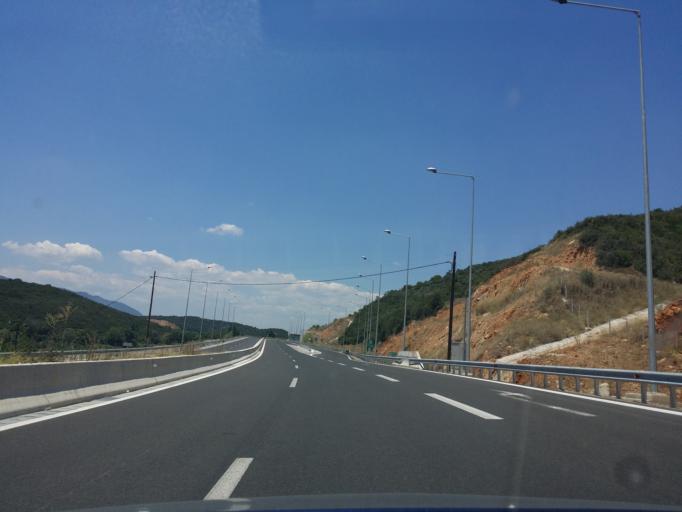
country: GR
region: Peloponnese
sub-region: Nomos Lakonias
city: Magoula
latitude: 37.1481
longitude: 22.3879
